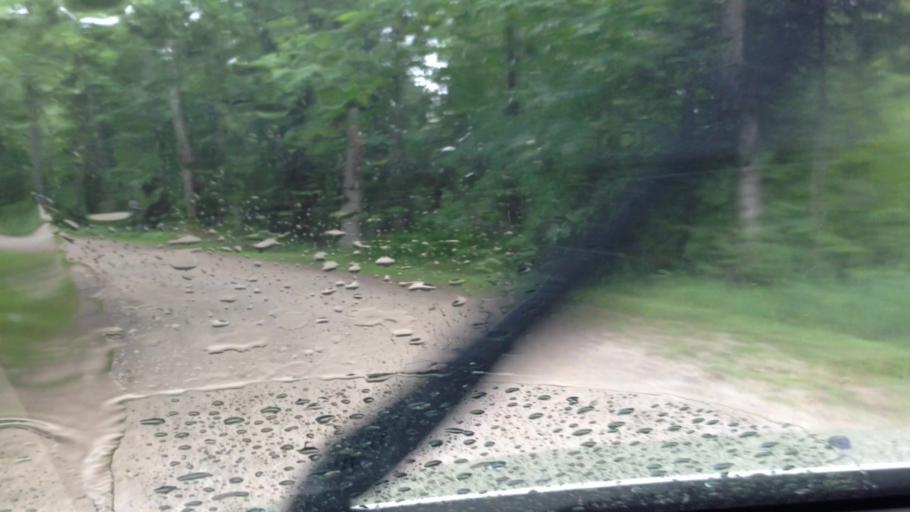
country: US
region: Michigan
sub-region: Menominee County
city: Menominee
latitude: 45.3945
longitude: -87.3651
